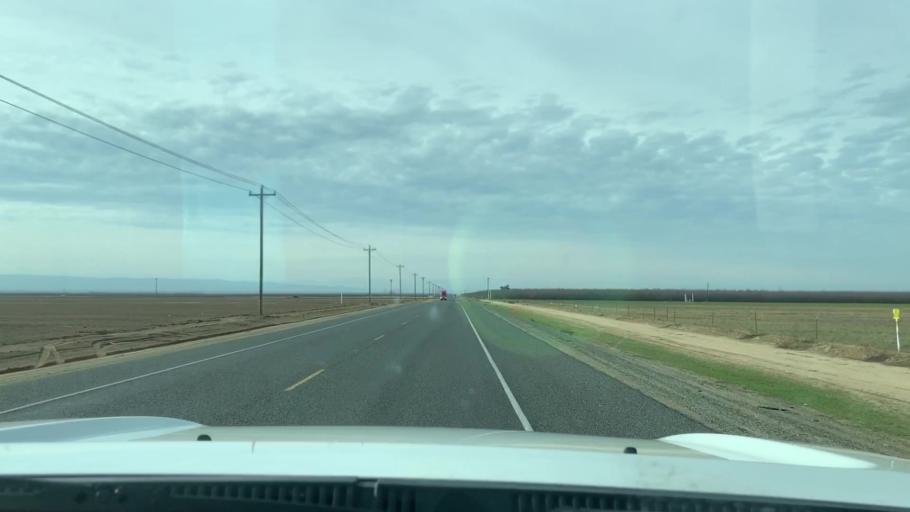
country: US
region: California
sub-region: Kern County
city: Lost Hills
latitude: 35.6013
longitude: -119.5492
